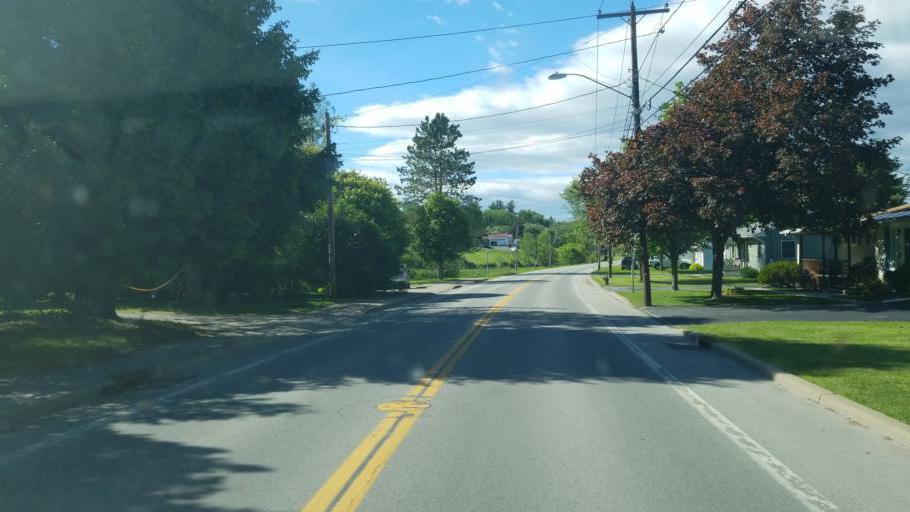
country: US
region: New York
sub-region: Montgomery County
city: Fort Plain
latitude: 42.9383
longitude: -74.6281
